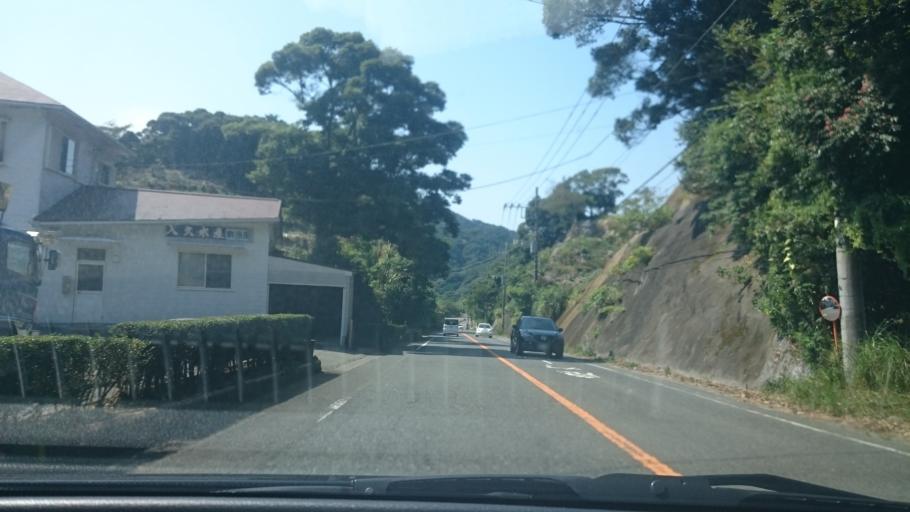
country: JP
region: Shizuoka
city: Heda
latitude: 34.8085
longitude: 138.7758
